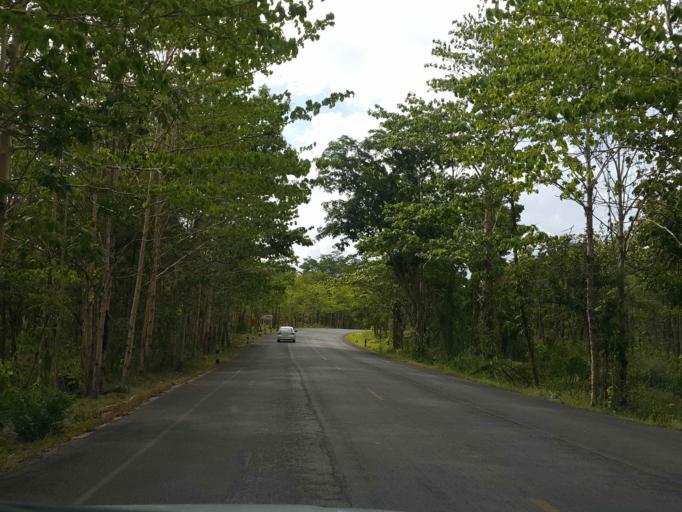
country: TH
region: Sukhothai
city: Thung Saliam
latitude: 17.4323
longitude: 99.3741
